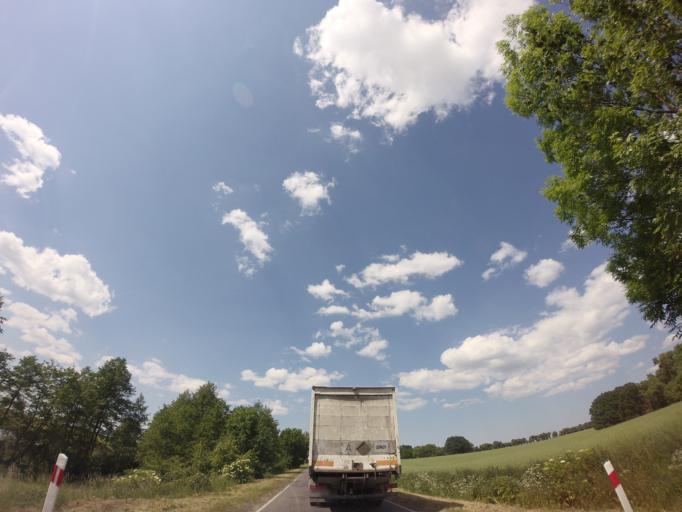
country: PL
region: West Pomeranian Voivodeship
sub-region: Powiat stargardzki
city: Dolice
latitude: 53.1306
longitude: 15.2533
